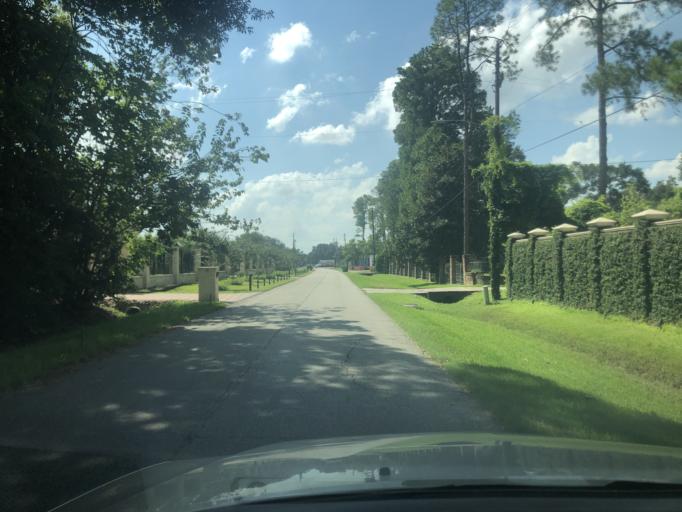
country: US
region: Texas
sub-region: Harris County
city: Bunker Hill Village
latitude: 29.7395
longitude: -95.5458
